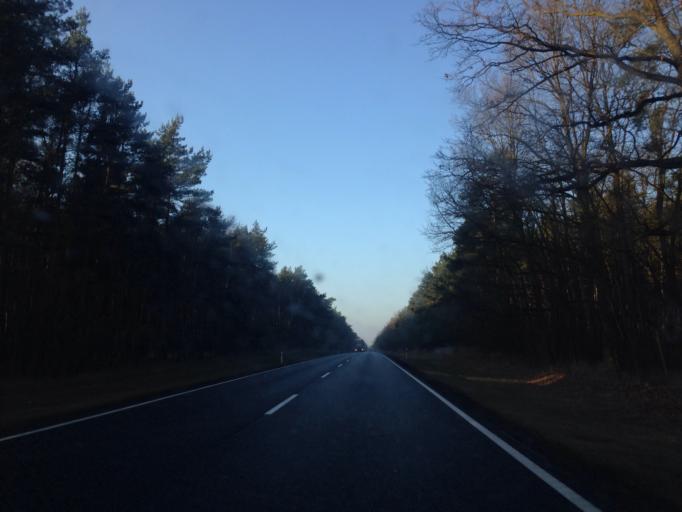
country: PL
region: Kujawsko-Pomorskie
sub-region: Powiat torunski
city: Zlawies Wielka
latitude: 53.0373
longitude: 18.3971
